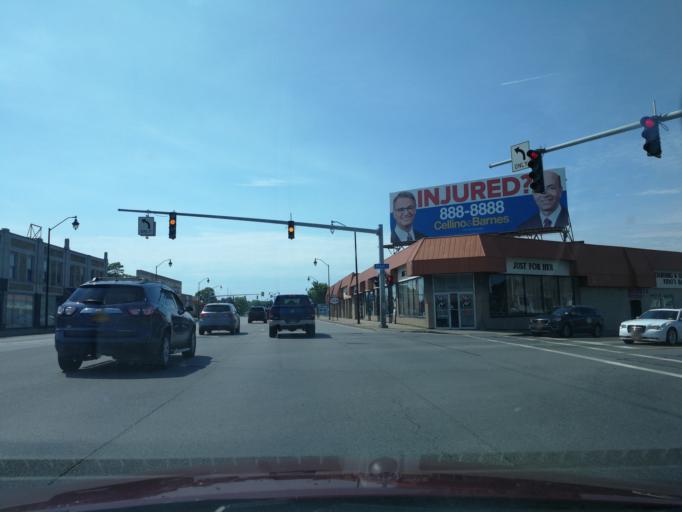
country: US
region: New York
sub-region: Monroe County
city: Rochester
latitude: 43.2006
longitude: -77.6386
